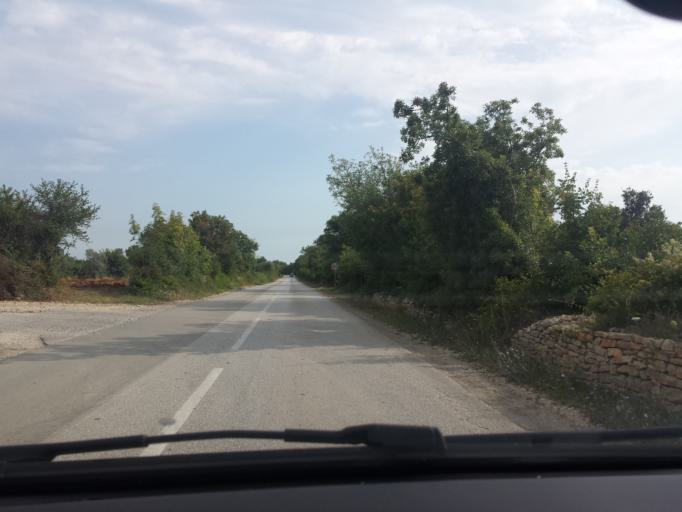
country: HR
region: Istarska
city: Galizana
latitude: 44.9099
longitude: 13.8563
